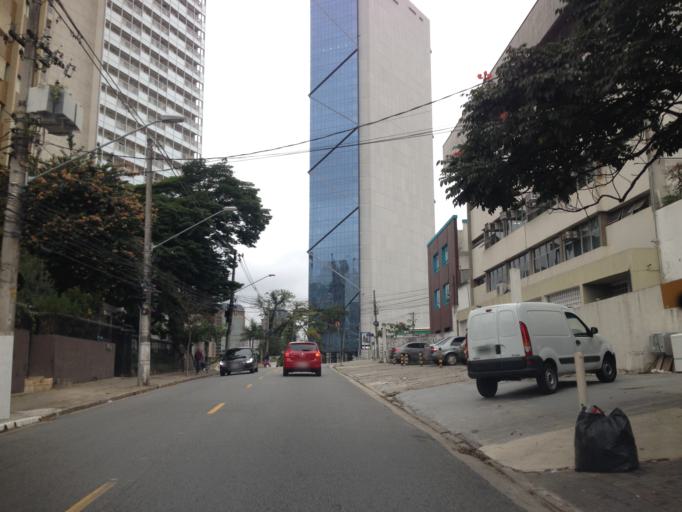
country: BR
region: Sao Paulo
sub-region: Taboao Da Serra
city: Taboao da Serra
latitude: -23.6149
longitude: -46.7024
